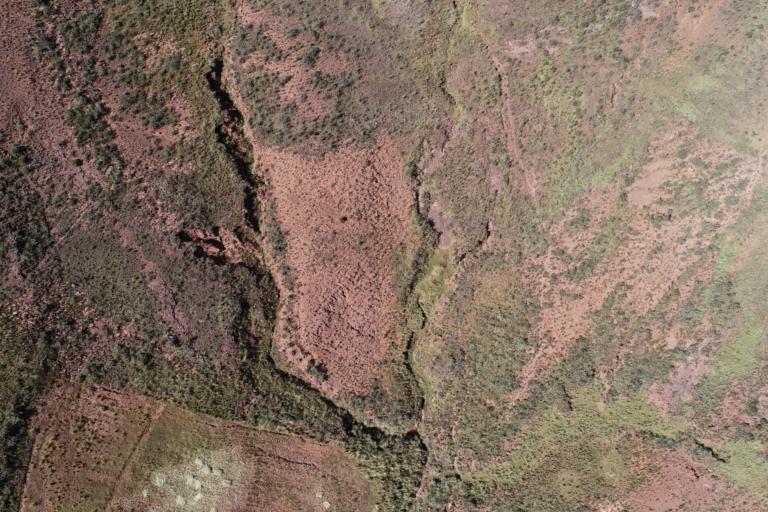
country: BO
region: La Paz
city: Tiahuanaco
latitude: -16.5975
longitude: -68.7592
